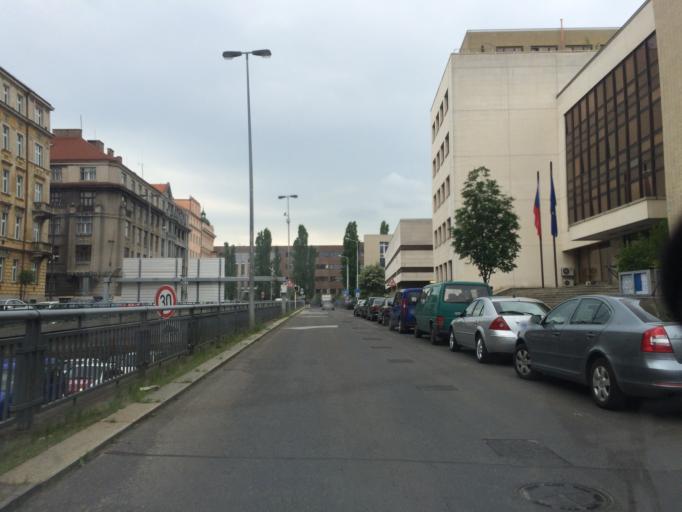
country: CZ
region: Praha
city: Prague
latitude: 50.0992
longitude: 14.4219
